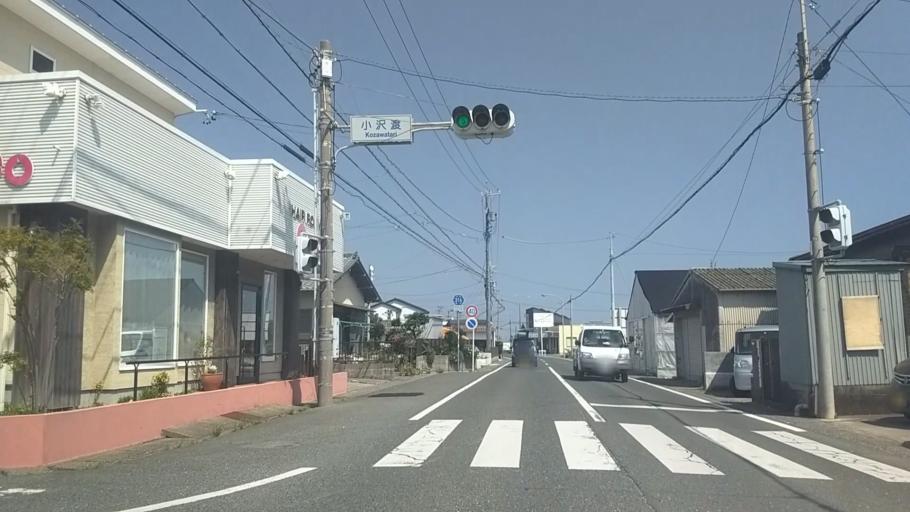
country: JP
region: Shizuoka
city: Hamamatsu
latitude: 34.6817
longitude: 137.6859
